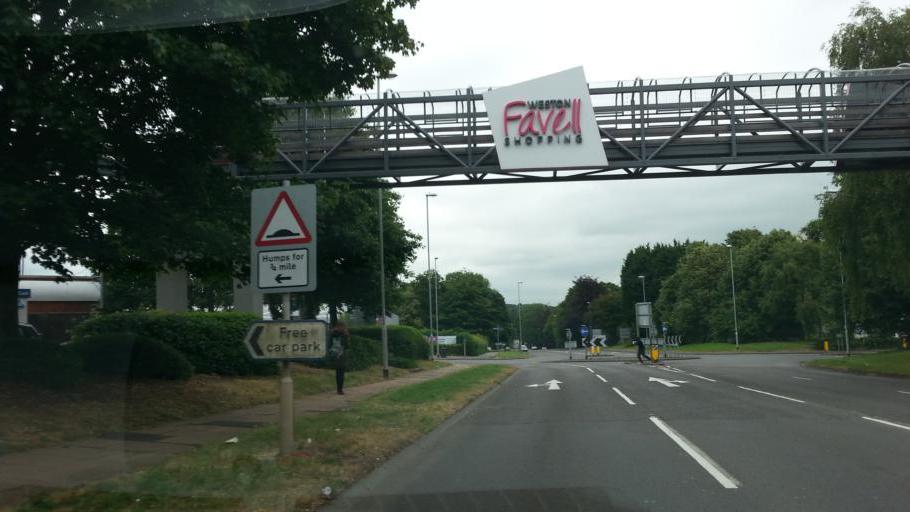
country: GB
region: England
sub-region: Northamptonshire
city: Northampton
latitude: 52.2558
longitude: -0.8358
